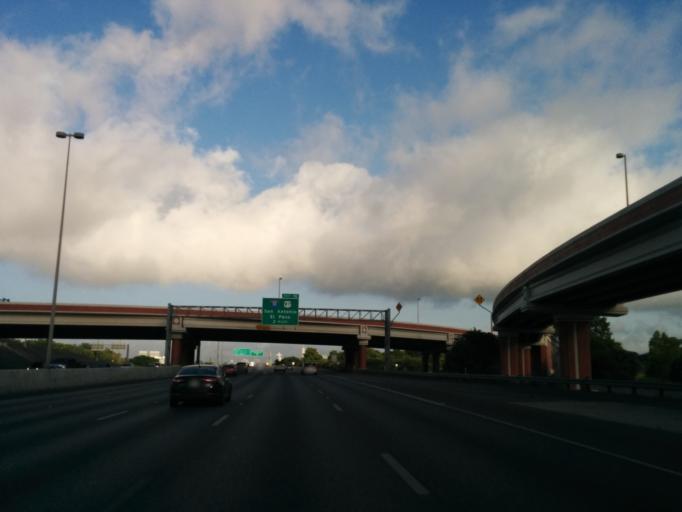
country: US
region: Texas
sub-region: Bexar County
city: Castle Hills
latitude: 29.5208
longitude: -98.5116
